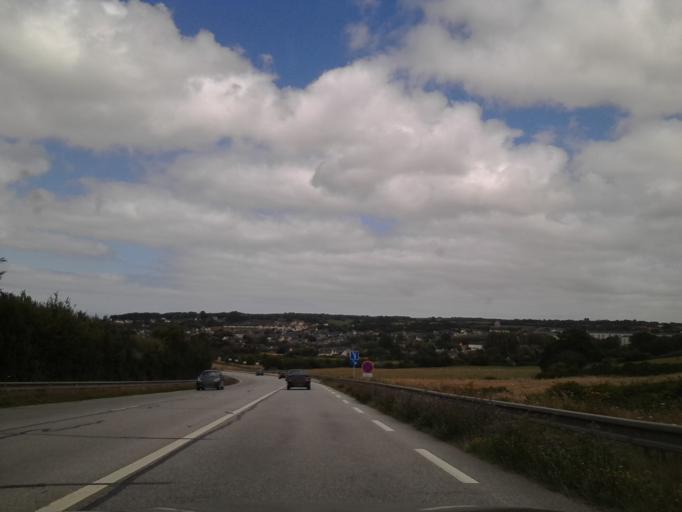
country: FR
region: Lower Normandy
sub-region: Departement de la Manche
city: Tourlaville
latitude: 49.6299
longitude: -1.5803
